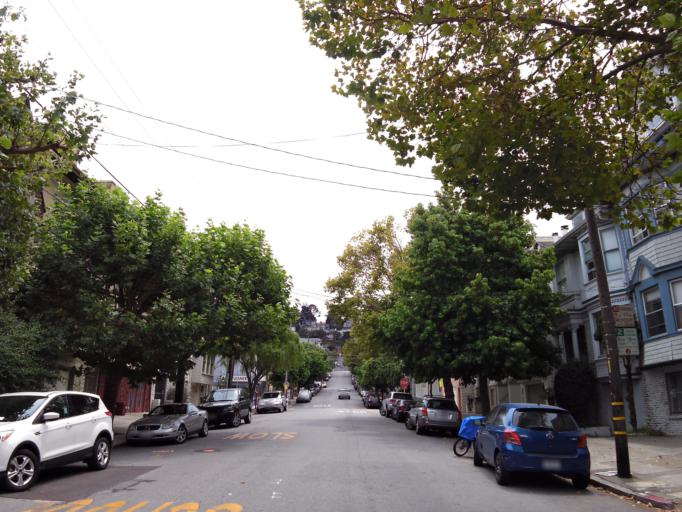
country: US
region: California
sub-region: San Francisco County
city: San Francisco
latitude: 37.7637
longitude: -122.4496
